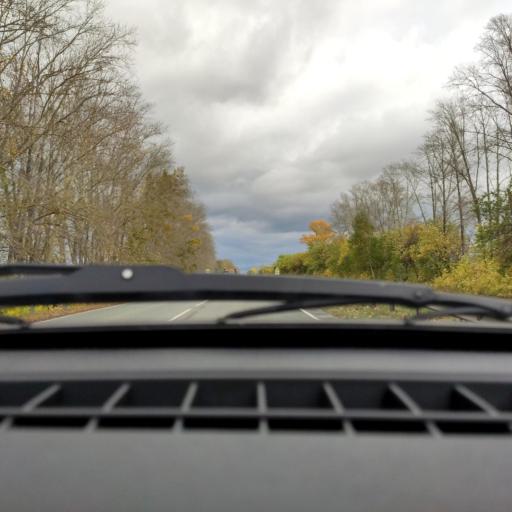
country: RU
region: Bashkortostan
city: Shafranovo
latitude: 54.0142
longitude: 54.8177
